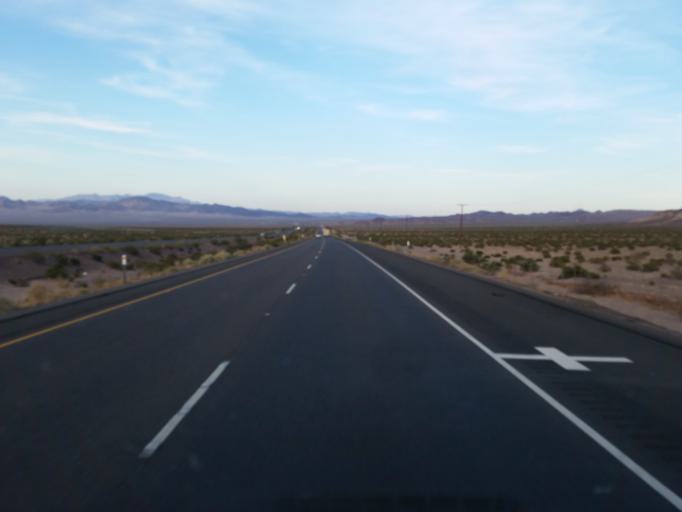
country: US
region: California
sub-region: San Bernardino County
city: Joshua Tree
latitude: 34.7262
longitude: -116.2418
